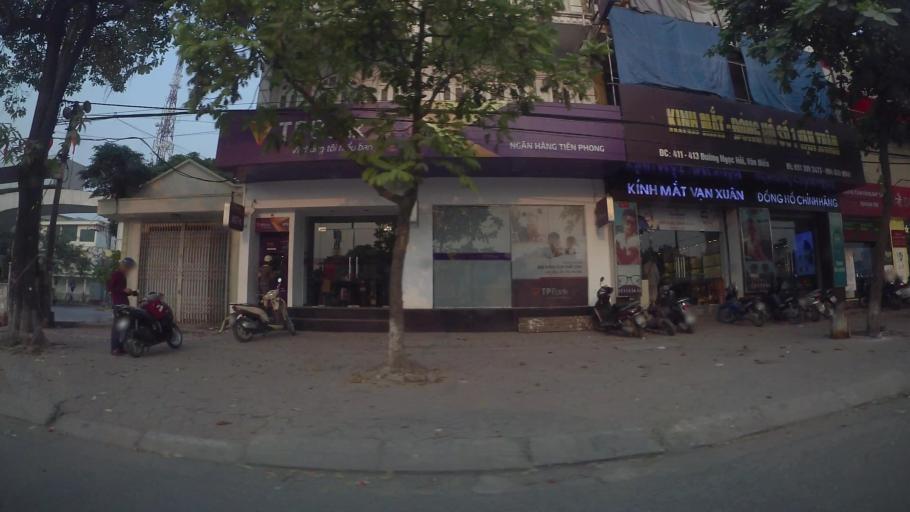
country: VN
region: Ha Noi
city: Van Dien
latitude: 20.9449
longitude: 105.8445
